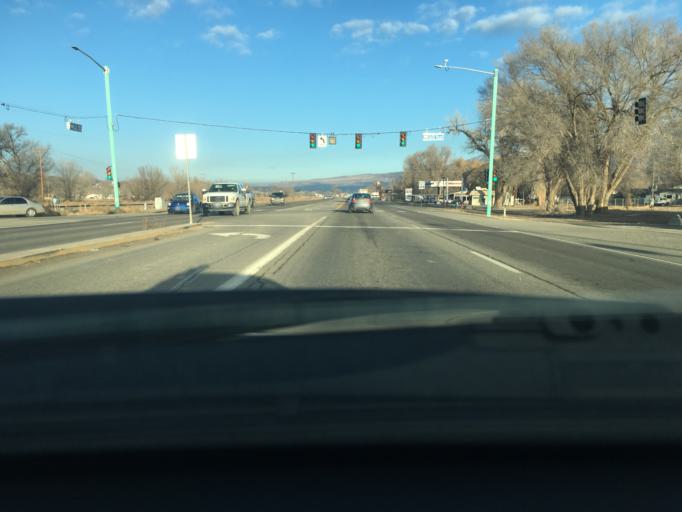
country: US
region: Colorado
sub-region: Delta County
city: Delta
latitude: 38.7251
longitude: -108.0640
